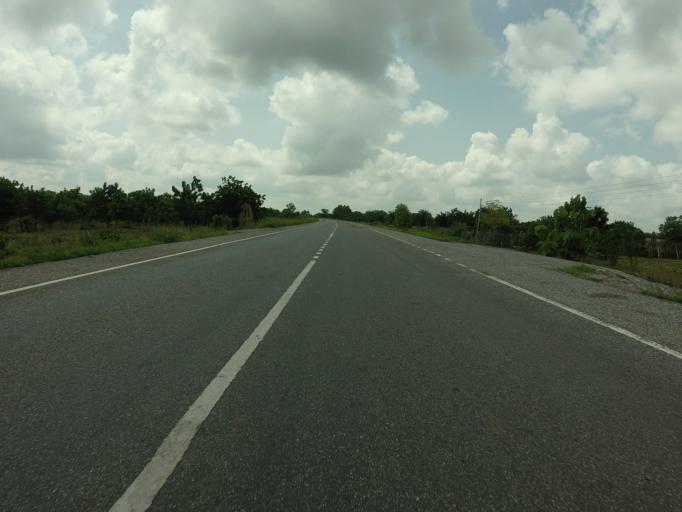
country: GH
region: Northern
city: Tamale
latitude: 9.1632
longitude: -1.4999
